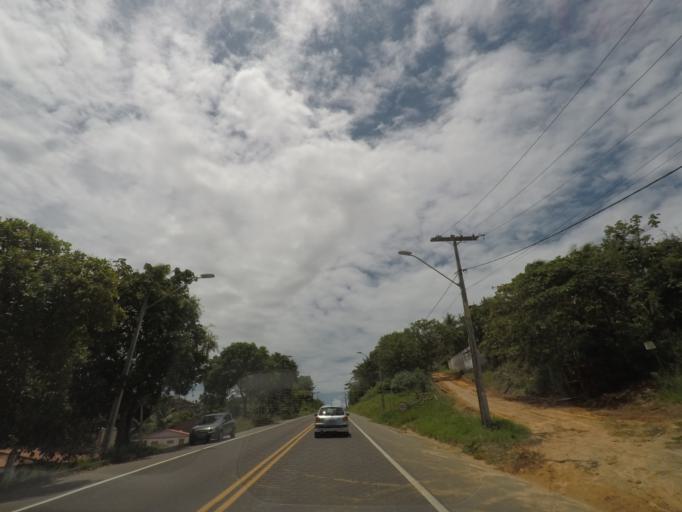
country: BR
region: Bahia
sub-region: Itaparica
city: Itaparica
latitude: -12.9379
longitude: -38.6264
